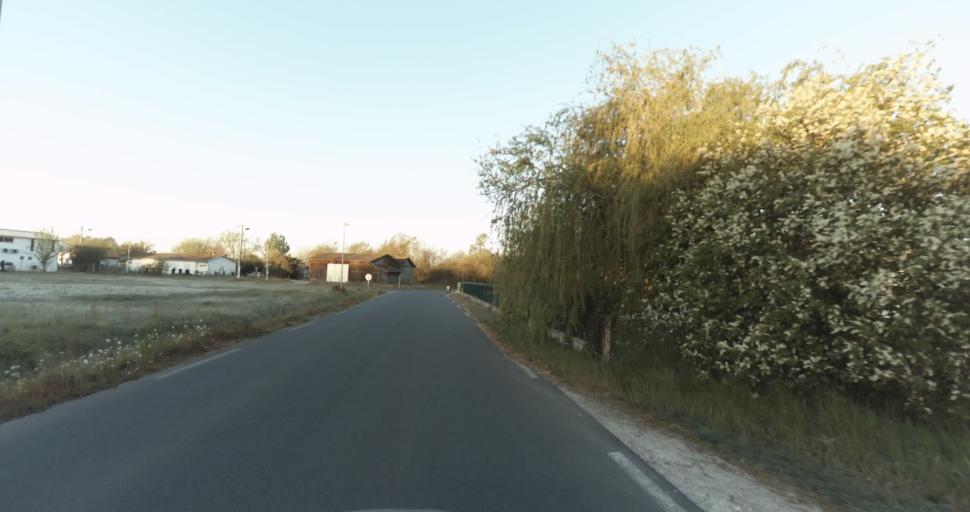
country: FR
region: Aquitaine
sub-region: Departement de la Gironde
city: Martignas-sur-Jalle
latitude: 44.8131
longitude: -0.7505
